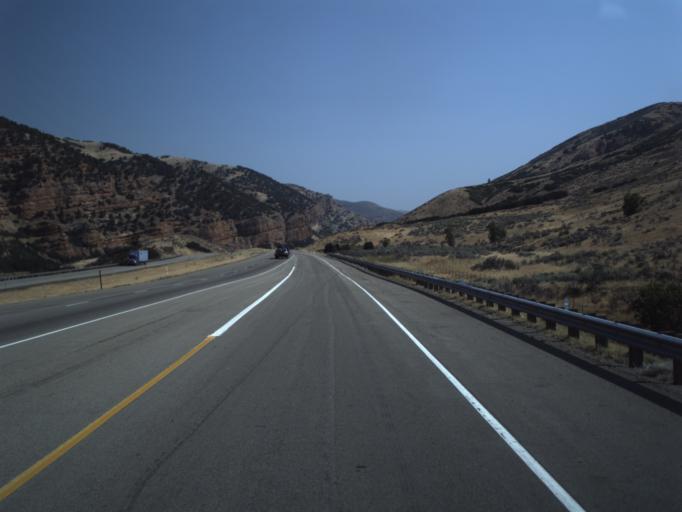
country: US
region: Utah
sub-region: Summit County
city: Coalville
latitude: 40.9913
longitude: -111.4014
